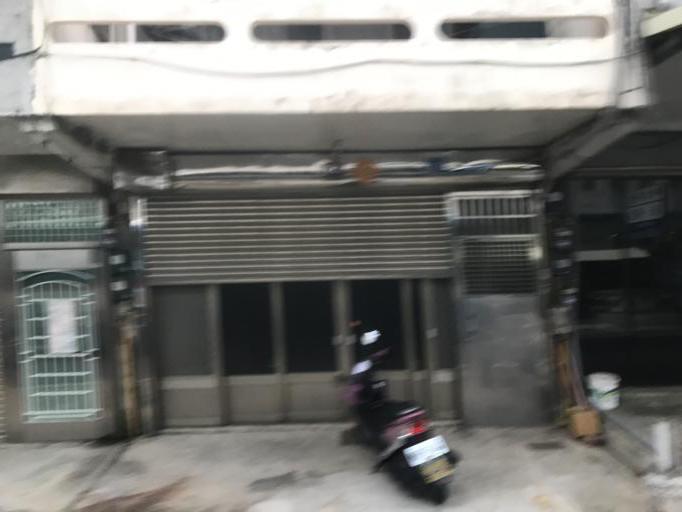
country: TW
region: Taiwan
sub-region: Hsinchu
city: Hsinchu
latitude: 24.7833
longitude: 120.9326
